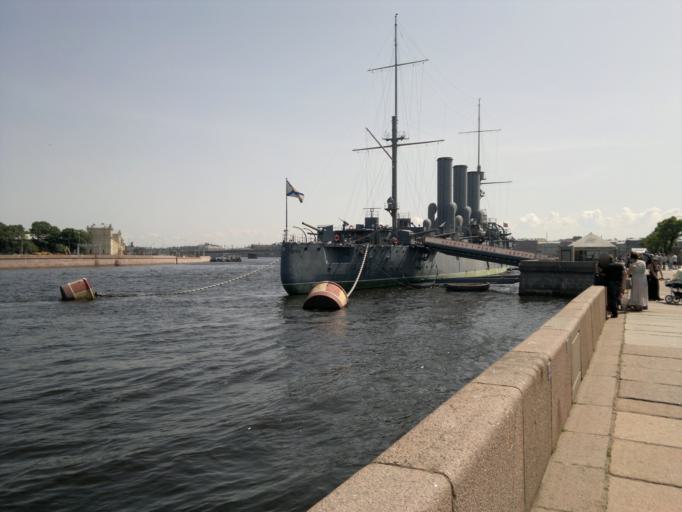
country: RU
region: St.-Petersburg
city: Petrogradka
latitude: 59.9560
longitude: 30.3365
